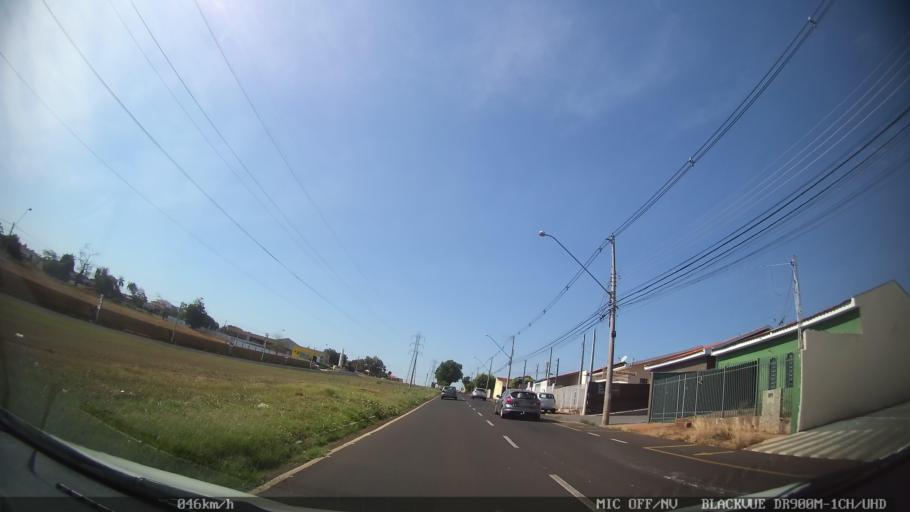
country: BR
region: Sao Paulo
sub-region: Sao Jose Do Rio Preto
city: Sao Jose do Rio Preto
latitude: -20.7918
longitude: -49.4217
